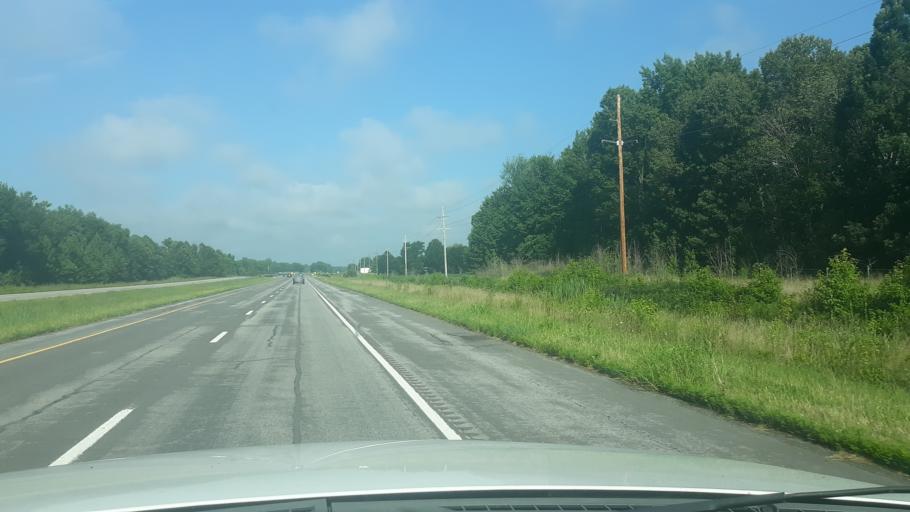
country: US
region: Illinois
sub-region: Saline County
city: Carrier Mills
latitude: 37.7336
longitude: -88.6643
